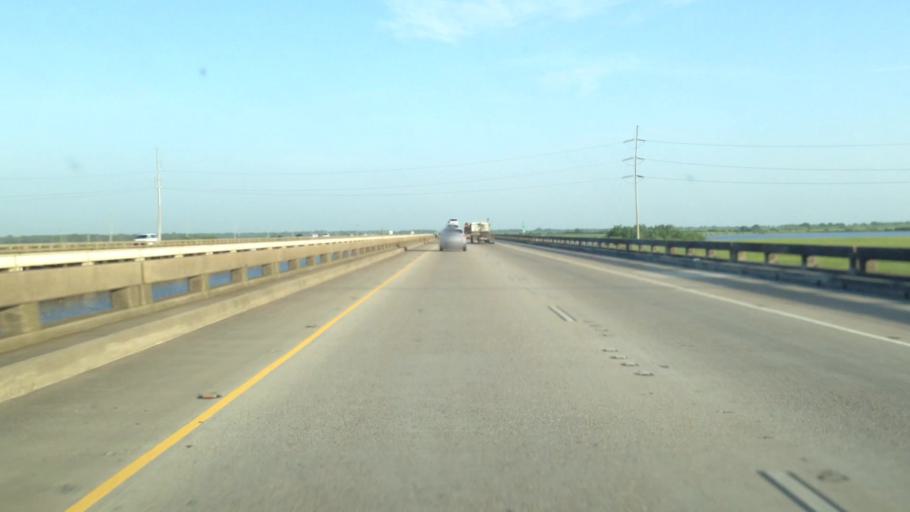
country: US
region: Louisiana
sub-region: Saint Charles Parish
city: New Sarpy
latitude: 30.0366
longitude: -90.3435
